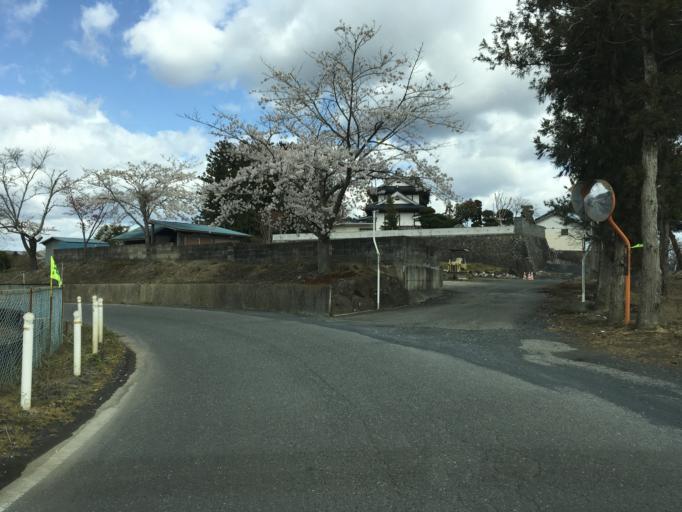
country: JP
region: Iwate
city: Ichinoseki
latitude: 38.7483
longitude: 141.2583
